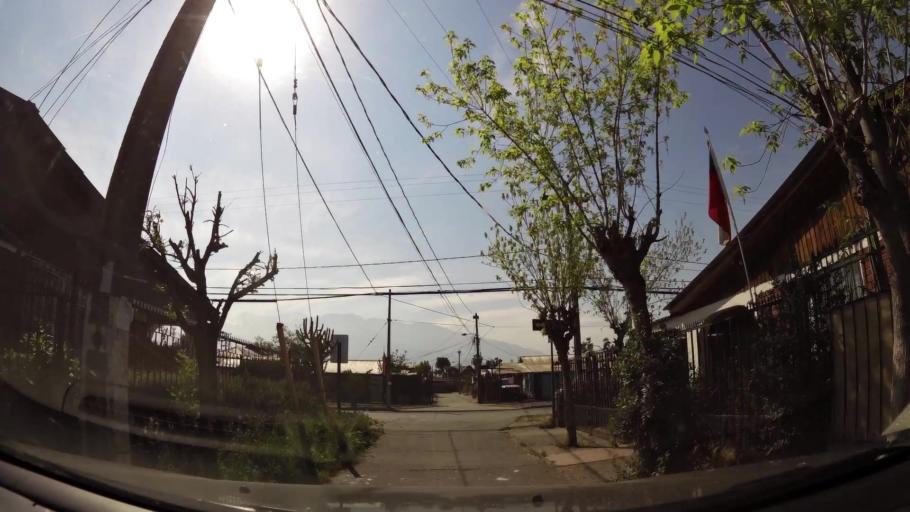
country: CL
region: Santiago Metropolitan
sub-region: Provincia de Cordillera
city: Puente Alto
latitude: -33.5700
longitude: -70.5897
